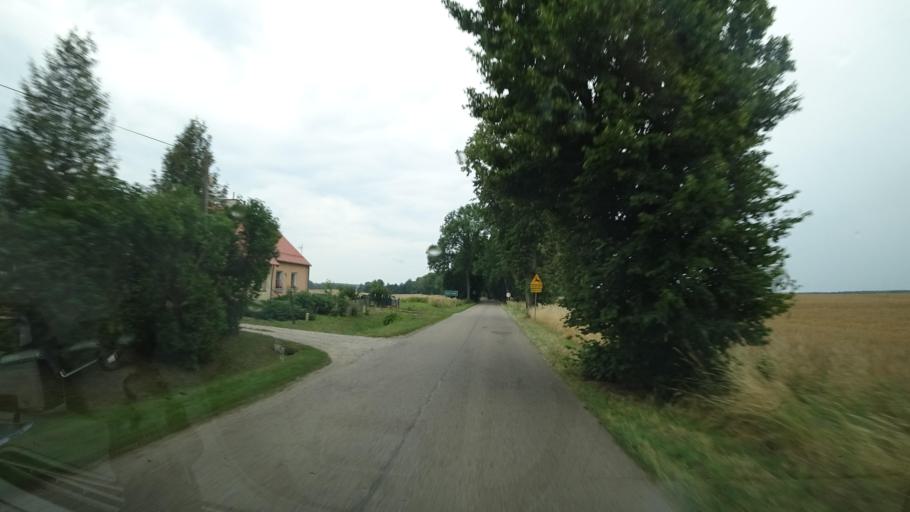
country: PL
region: Warmian-Masurian Voivodeship
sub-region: Powiat gizycki
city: Ryn
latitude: 53.9229
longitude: 21.5532
